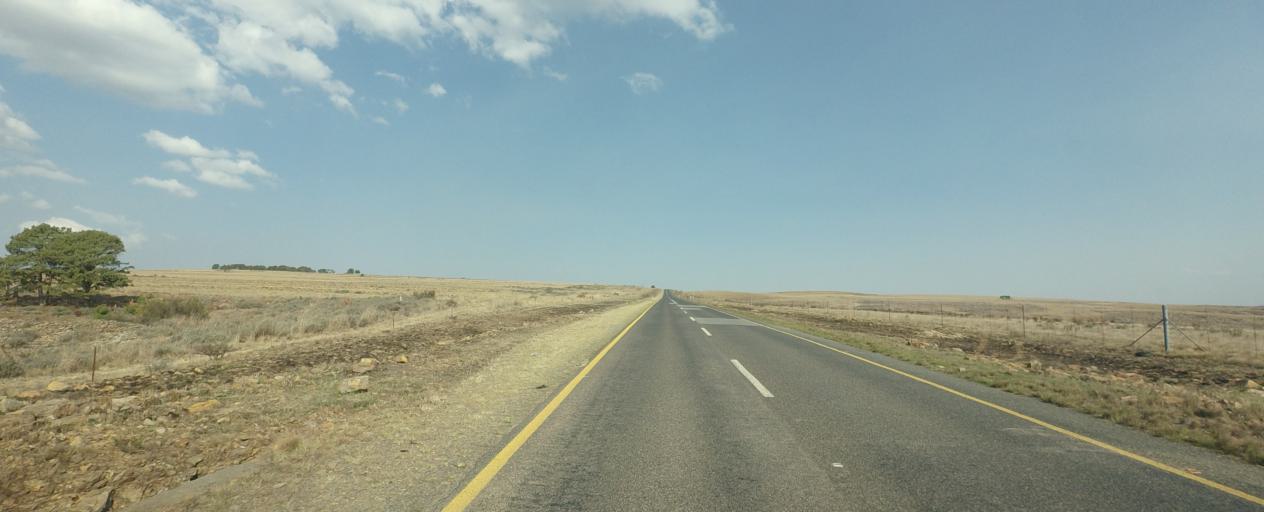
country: ZA
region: Mpumalanga
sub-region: Ehlanzeni District
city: Lydenburg
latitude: -25.1225
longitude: 30.5806
